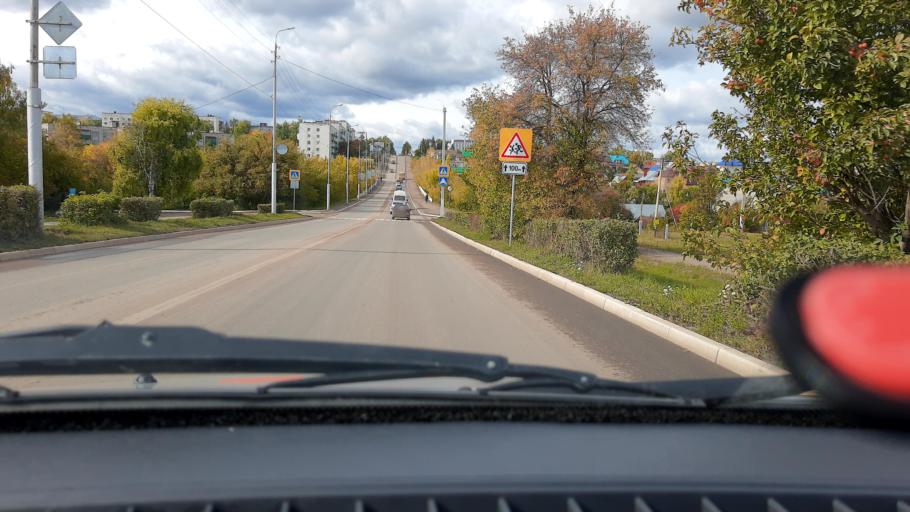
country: RU
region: Bashkortostan
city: Belebey
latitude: 54.1006
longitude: 54.1173
